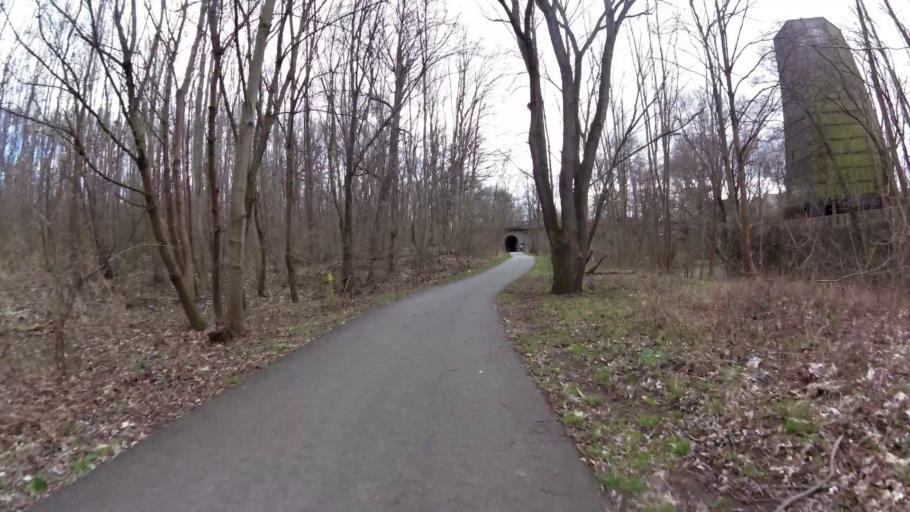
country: DE
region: Thuringia
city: Weimar
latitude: 50.9854
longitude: 11.3339
